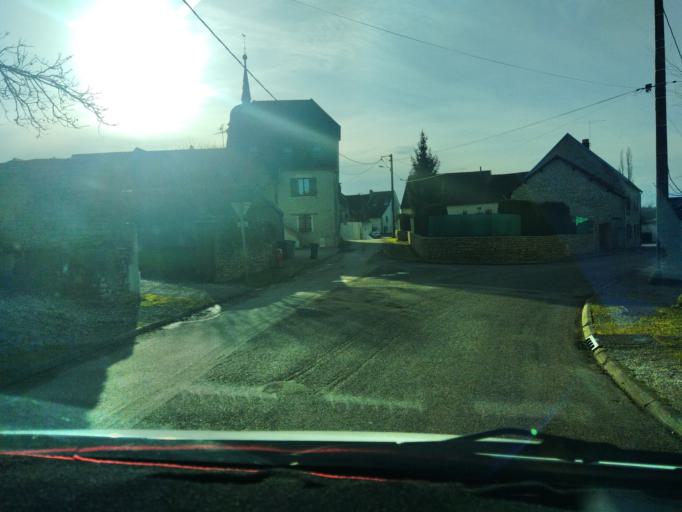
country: FR
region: Franche-Comte
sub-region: Departement de la Haute-Saone
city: Marnay
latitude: 47.3211
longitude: 5.6844
